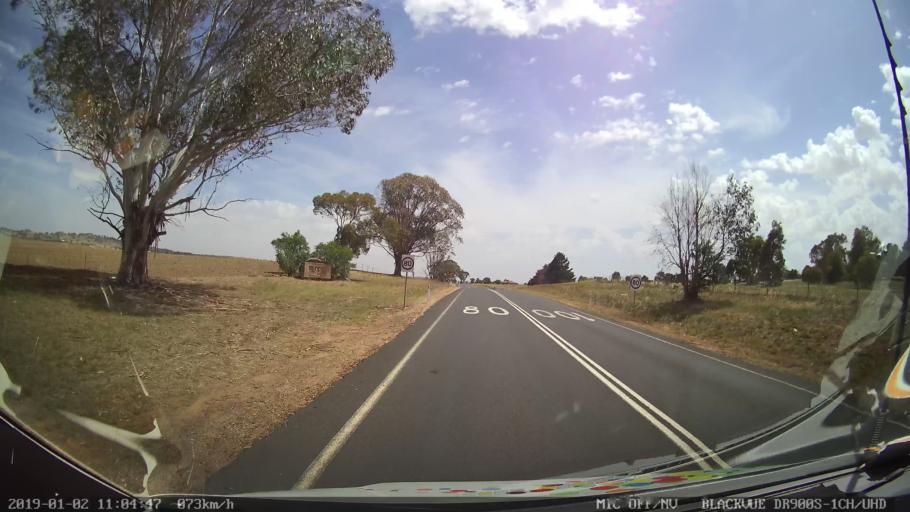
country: AU
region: New South Wales
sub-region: Young
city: Young
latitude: -34.5725
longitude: 148.3538
